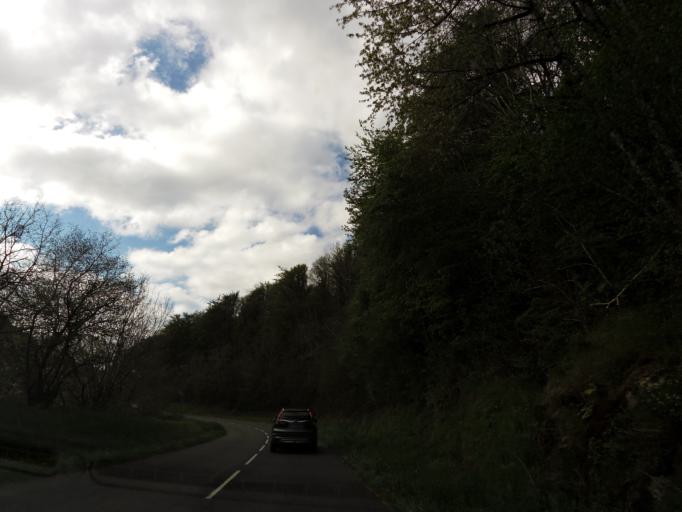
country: FR
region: Midi-Pyrenees
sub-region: Departement du Tarn
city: Soreze
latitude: 43.4188
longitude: 2.0615
